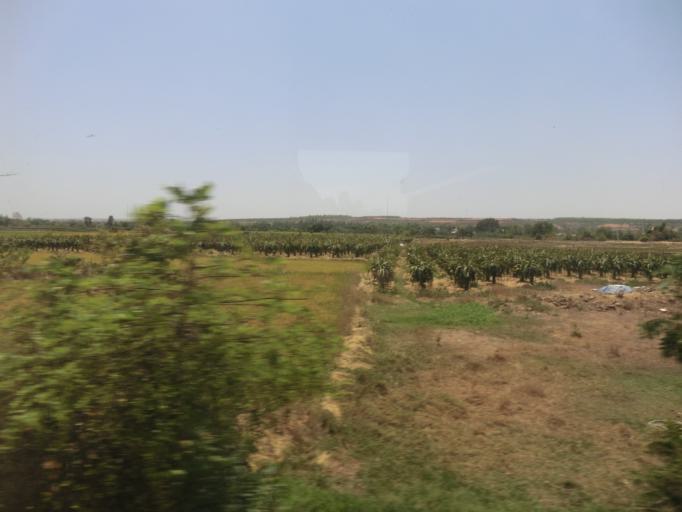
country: VN
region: Binh Thuan
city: Cho Lau
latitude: 11.2238
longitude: 108.4101
